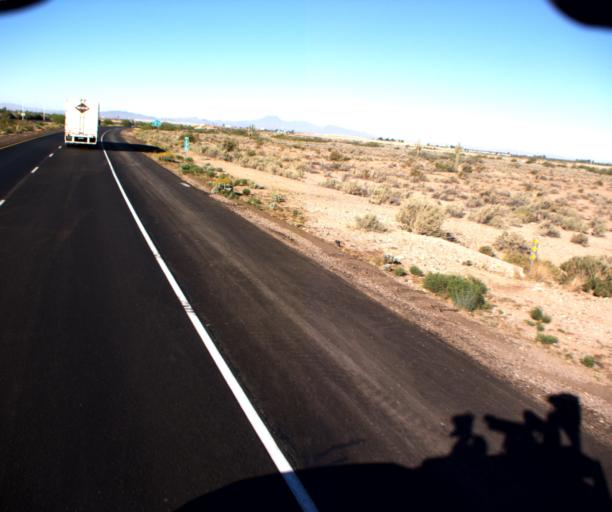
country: US
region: Arizona
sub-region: Pinal County
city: Casa Grande
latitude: 32.8311
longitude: -111.7326
